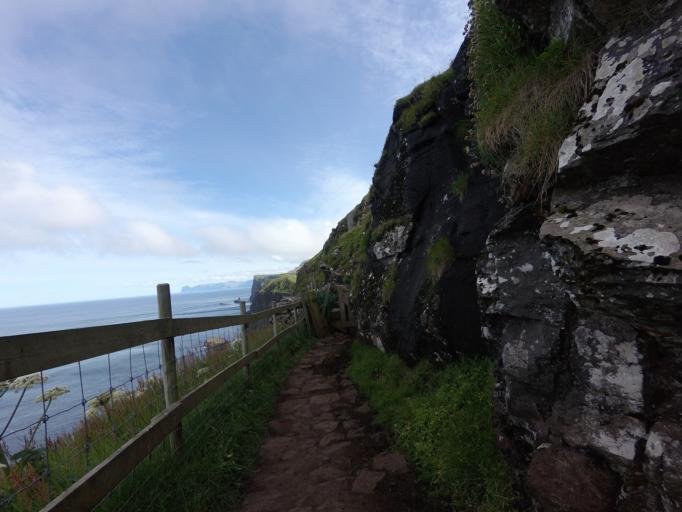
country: FO
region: Vagar
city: Sorvagur
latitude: 62.1026
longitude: -7.6611
